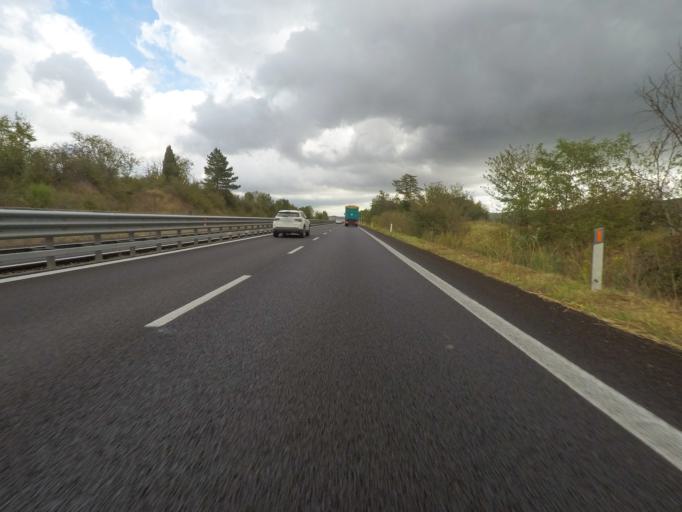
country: IT
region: Tuscany
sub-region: Provincia di Siena
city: Arbia
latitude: 43.3066
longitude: 11.4424
